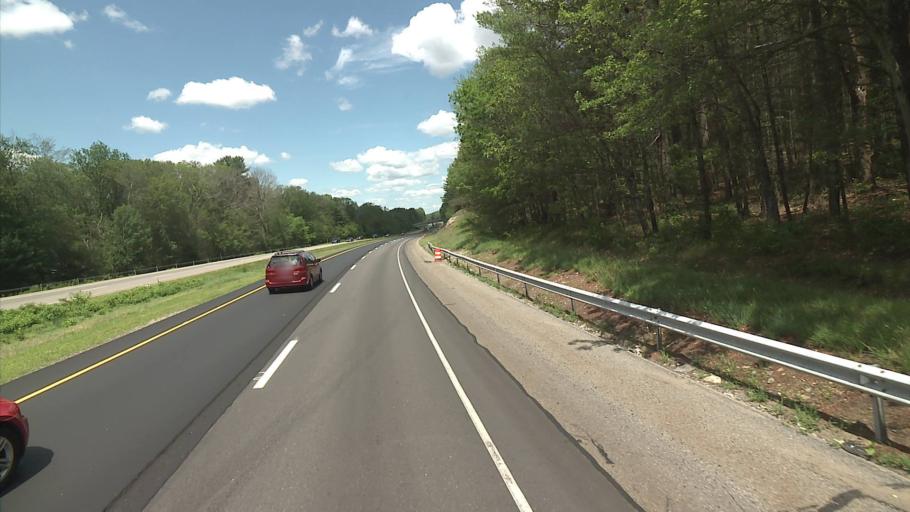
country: US
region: Connecticut
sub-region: Windham County
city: Killingly Center
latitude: 41.8280
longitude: -71.8740
